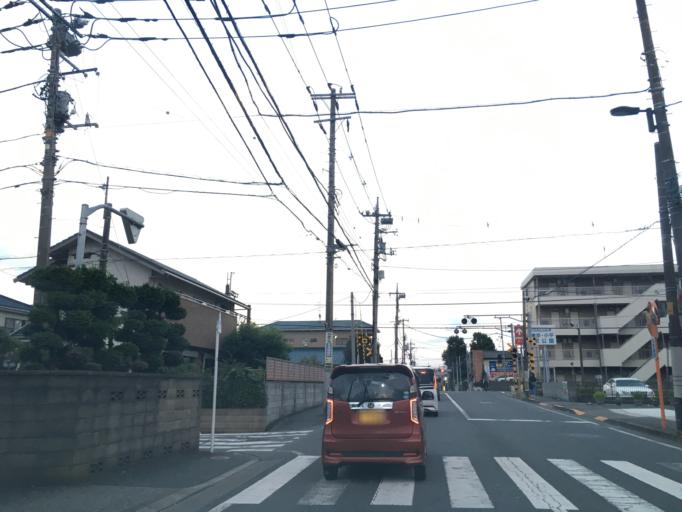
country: JP
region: Tokyo
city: Higashimurayama-shi
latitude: 35.7305
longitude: 139.4618
